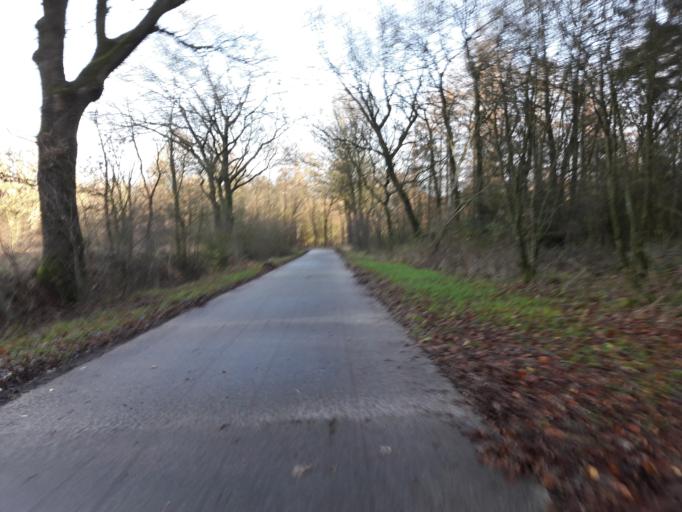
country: NL
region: Drenthe
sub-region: Gemeente Borger-Odoorn
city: Borger
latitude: 52.9331
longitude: 6.7065
